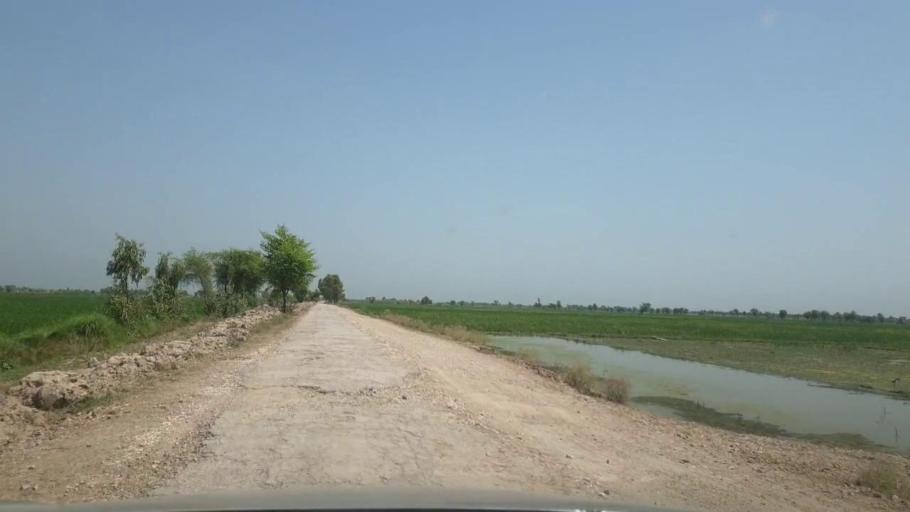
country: PK
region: Sindh
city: Warah
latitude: 27.5091
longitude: 67.7705
